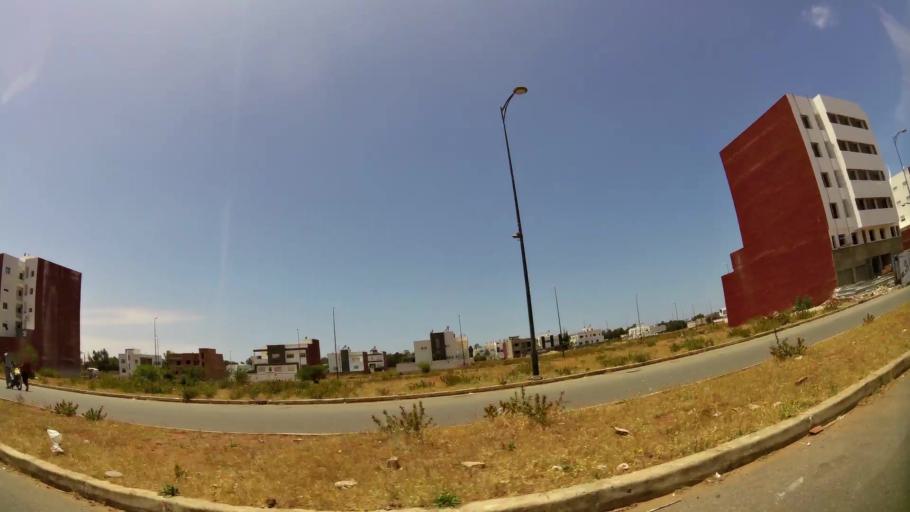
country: MA
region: Gharb-Chrarda-Beni Hssen
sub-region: Kenitra Province
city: Kenitra
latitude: 34.2668
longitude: -6.6266
